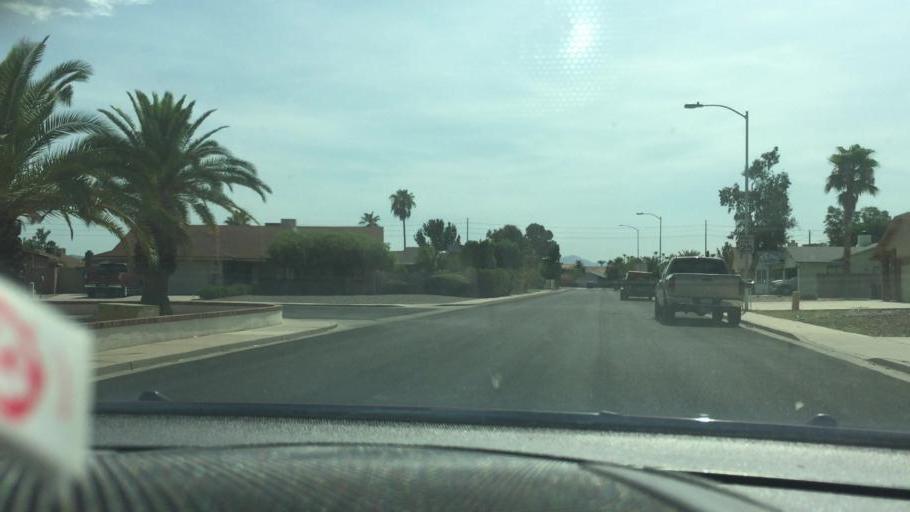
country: US
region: Arizona
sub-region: Maricopa County
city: Gilbert
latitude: 33.4016
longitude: -111.7132
